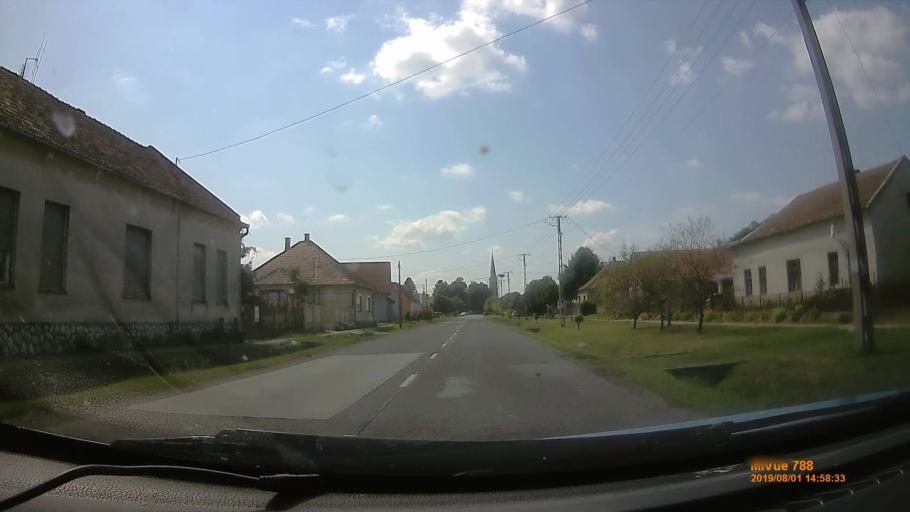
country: HU
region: Baranya
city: Sellye
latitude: 45.8805
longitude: 17.9157
